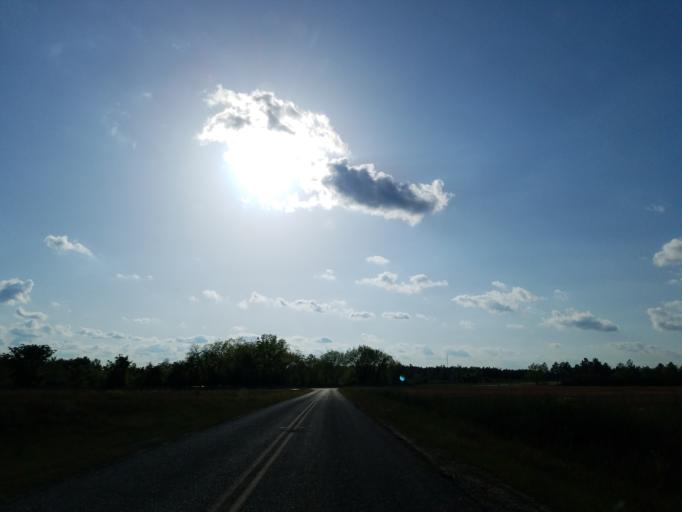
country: US
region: Georgia
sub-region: Turner County
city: Ashburn
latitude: 31.6092
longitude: -83.5959
